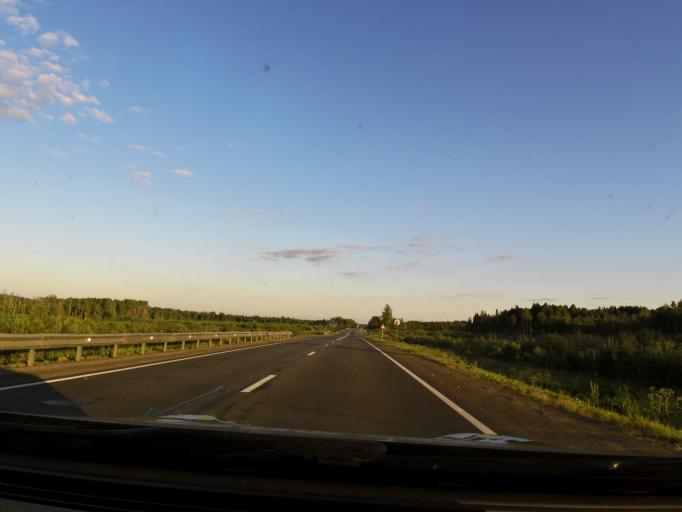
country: RU
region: Jaroslavl
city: Prechistoye
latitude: 58.5758
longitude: 40.3522
